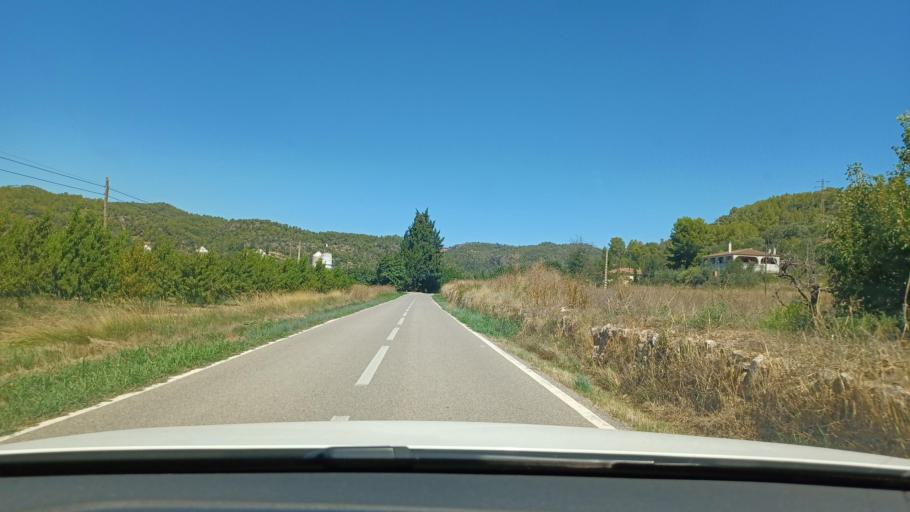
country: ES
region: Catalonia
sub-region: Provincia de Tarragona
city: Benifallet
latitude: 40.9638
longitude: 0.5139
